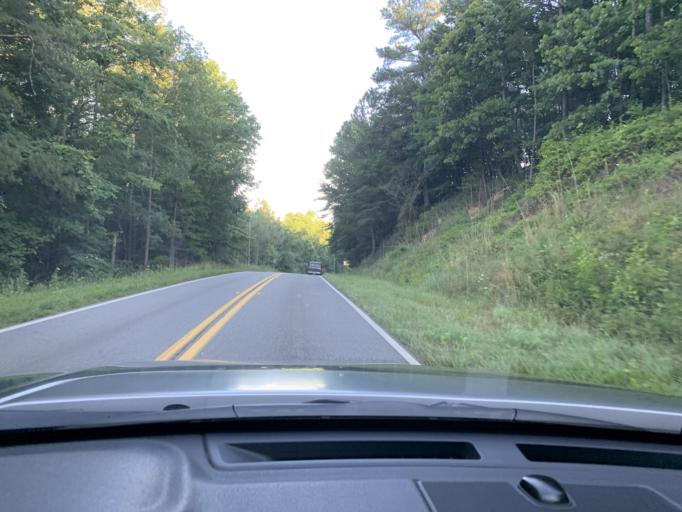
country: US
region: Georgia
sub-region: Bartow County
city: Rydal
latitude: 34.2697
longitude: -84.7243
